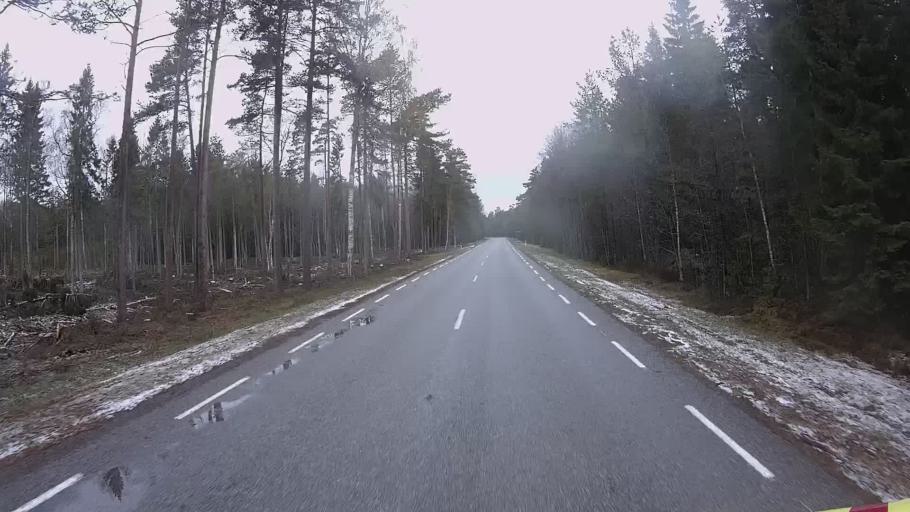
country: EE
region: Hiiumaa
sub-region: Kaerdla linn
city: Kardla
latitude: 59.0474
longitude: 22.6814
